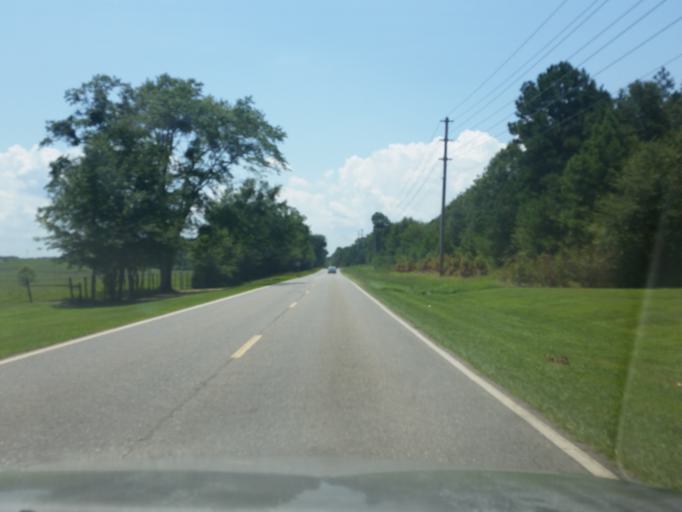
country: US
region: Alabama
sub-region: Baldwin County
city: Robertsdale
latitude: 30.6260
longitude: -87.6577
